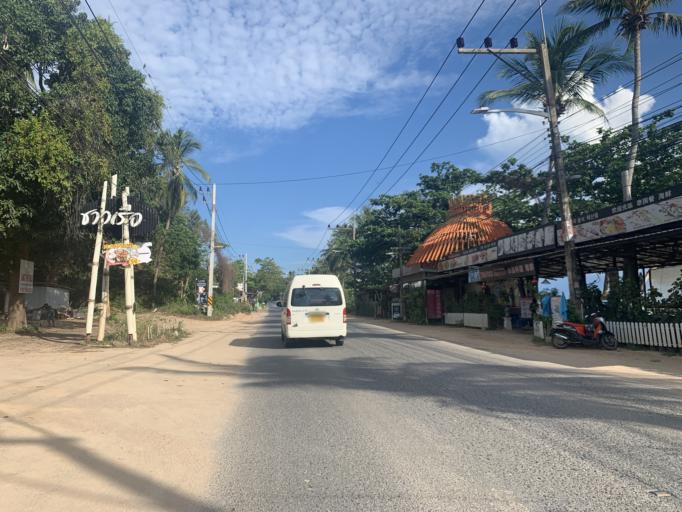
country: TH
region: Surat Thani
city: Ko Samui
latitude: 9.5589
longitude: 100.0452
